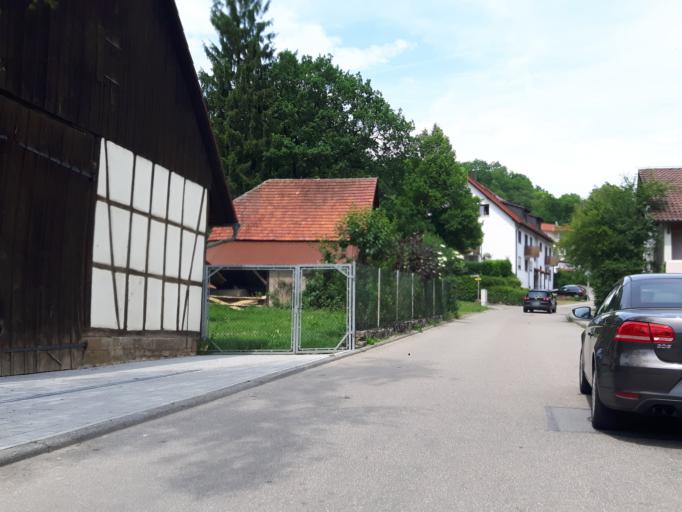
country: DE
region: Baden-Wuerttemberg
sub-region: Regierungsbezirk Stuttgart
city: Jagsthausen
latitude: 49.2795
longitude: 9.4800
